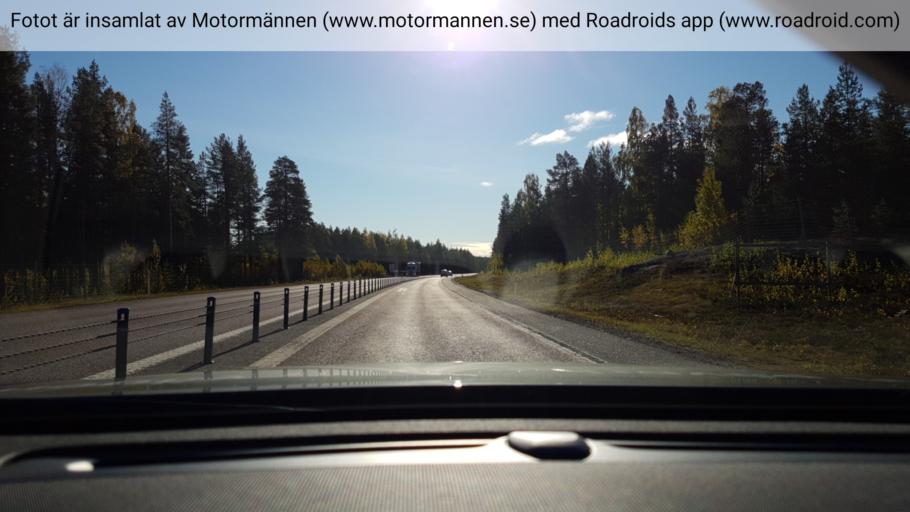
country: SE
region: Vaesterbotten
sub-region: Skelleftea Kommun
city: Burea
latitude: 64.6370
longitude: 21.1697
